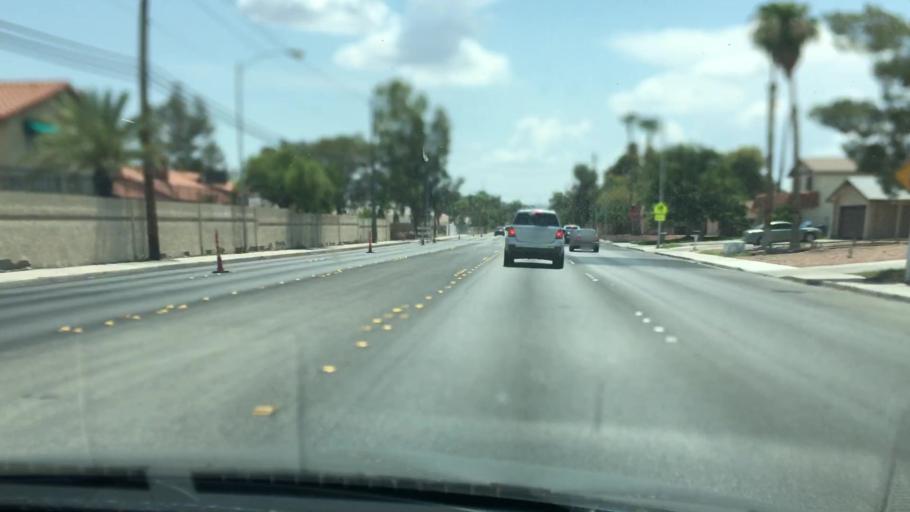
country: US
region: Nevada
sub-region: Clark County
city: Whitney
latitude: 36.0903
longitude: -115.0915
